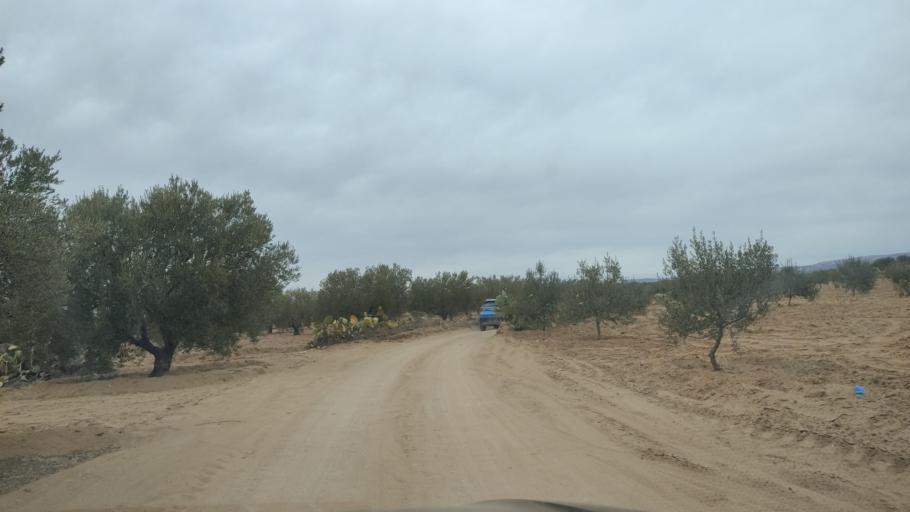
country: TN
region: Al Qasrayn
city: Kasserine
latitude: 35.2273
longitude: 8.9165
